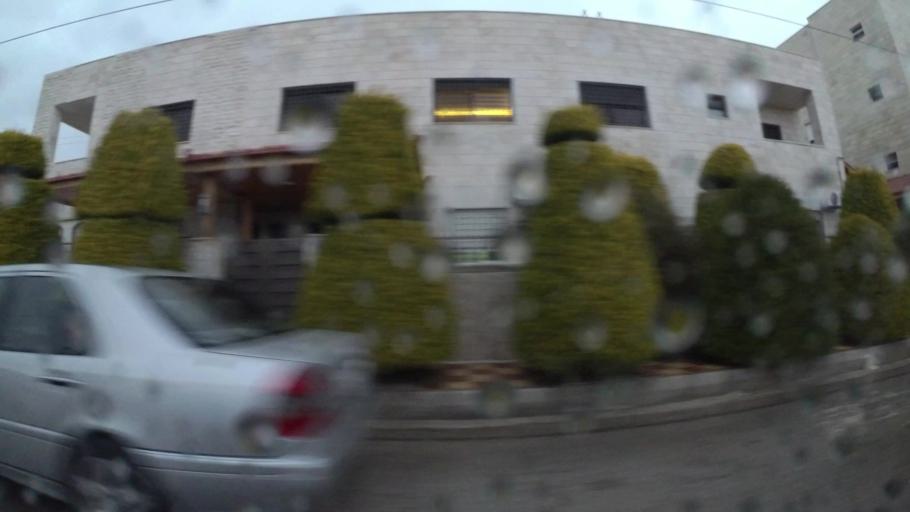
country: JO
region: Amman
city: Umm as Summaq
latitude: 31.9023
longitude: 35.8541
